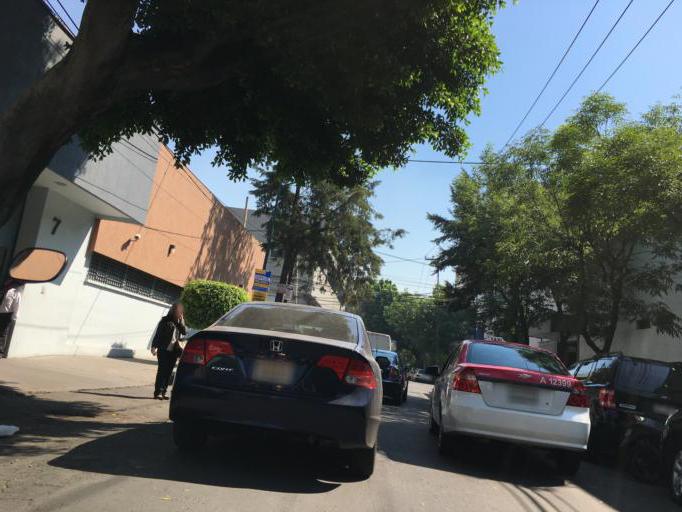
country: MX
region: Mexico City
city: Miguel Hidalgo
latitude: 19.4372
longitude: -99.1744
